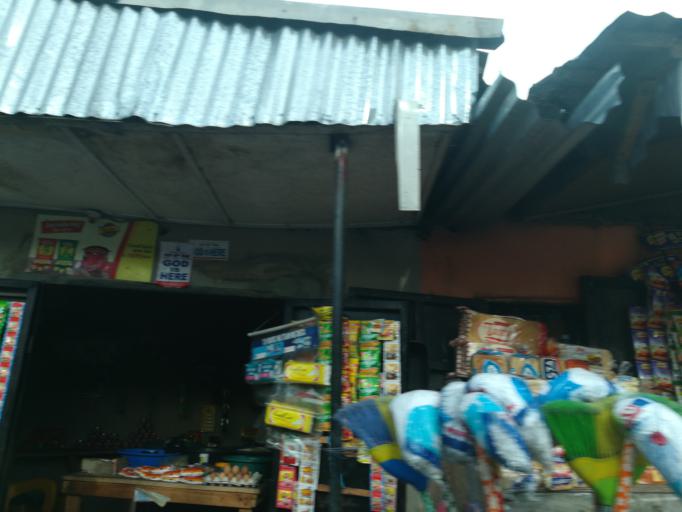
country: NG
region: Rivers
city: Port Harcourt
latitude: 4.8087
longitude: 6.9995
